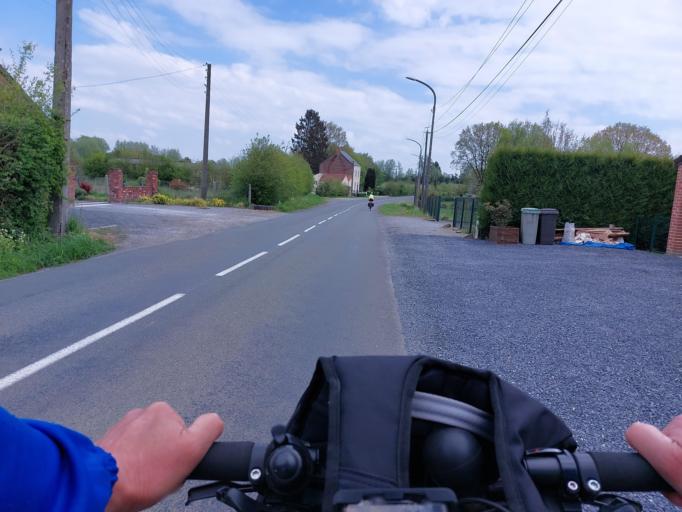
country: FR
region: Nord-Pas-de-Calais
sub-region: Departement du Nord
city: Hautmont
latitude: 50.2701
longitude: 3.8917
